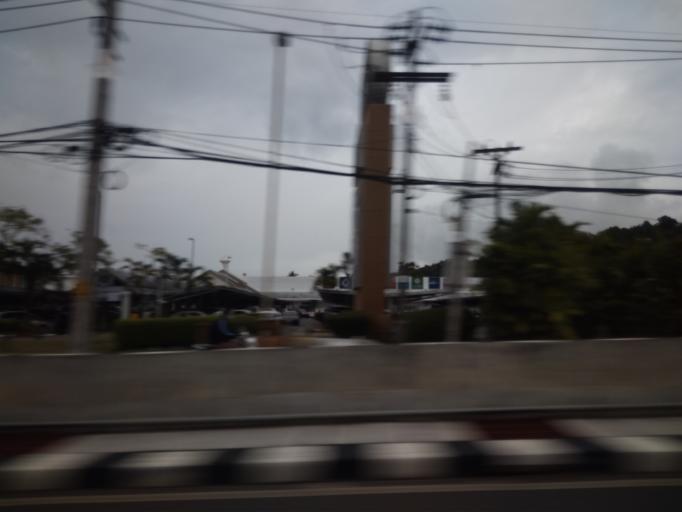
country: TH
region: Phuket
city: Wichit
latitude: 7.9035
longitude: 98.3678
